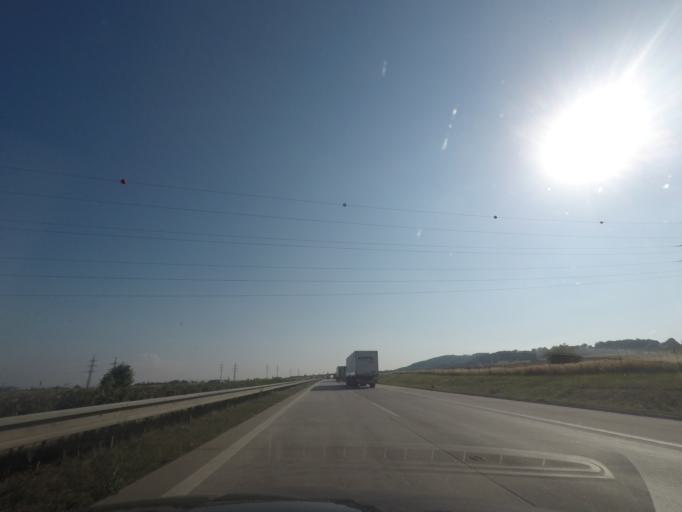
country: CZ
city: Fulnek
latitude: 49.6753
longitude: 17.9296
